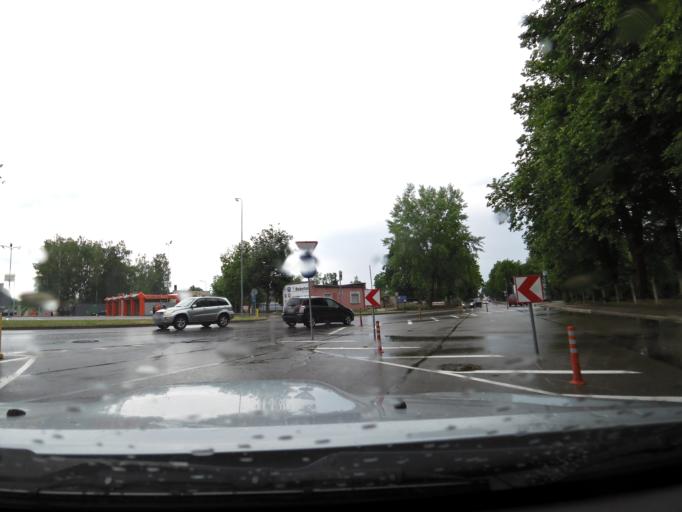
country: LT
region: Marijampoles apskritis
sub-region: Marijampole Municipality
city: Marijampole
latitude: 54.5463
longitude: 23.3477
